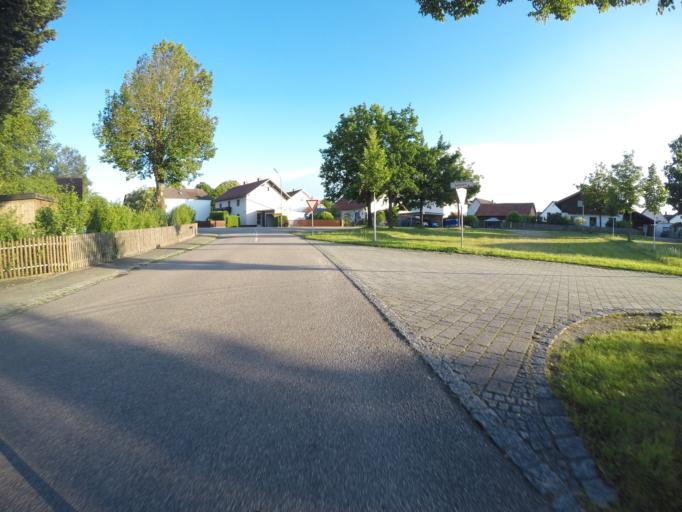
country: DE
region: Bavaria
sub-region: Lower Bavaria
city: Reisbach
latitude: 48.5727
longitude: 12.6238
